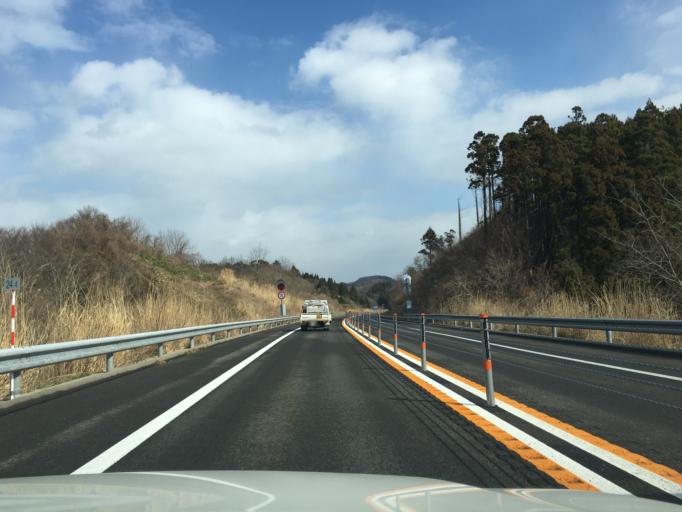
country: JP
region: Akita
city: Akita Shi
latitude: 39.4824
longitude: 140.0530
